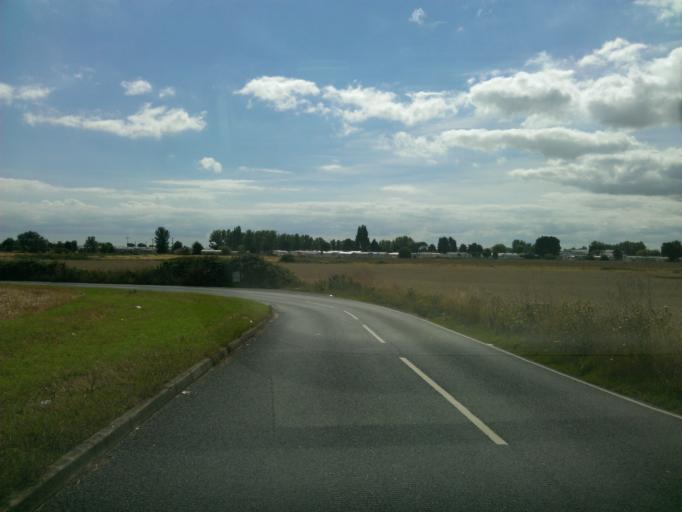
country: GB
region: England
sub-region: Essex
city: Saint Osyth
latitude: 51.7828
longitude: 1.0867
